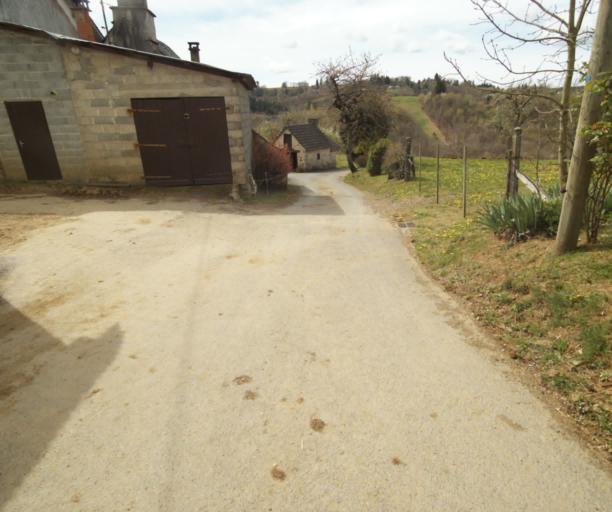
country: FR
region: Limousin
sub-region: Departement de la Correze
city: Laguenne
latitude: 45.2133
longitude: 1.8472
